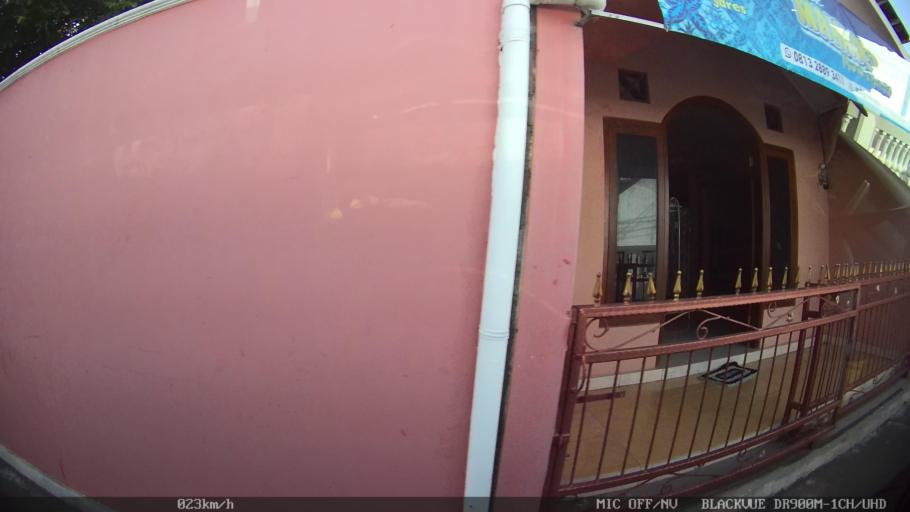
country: ID
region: Daerah Istimewa Yogyakarta
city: Sewon
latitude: -7.8332
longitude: 110.3965
